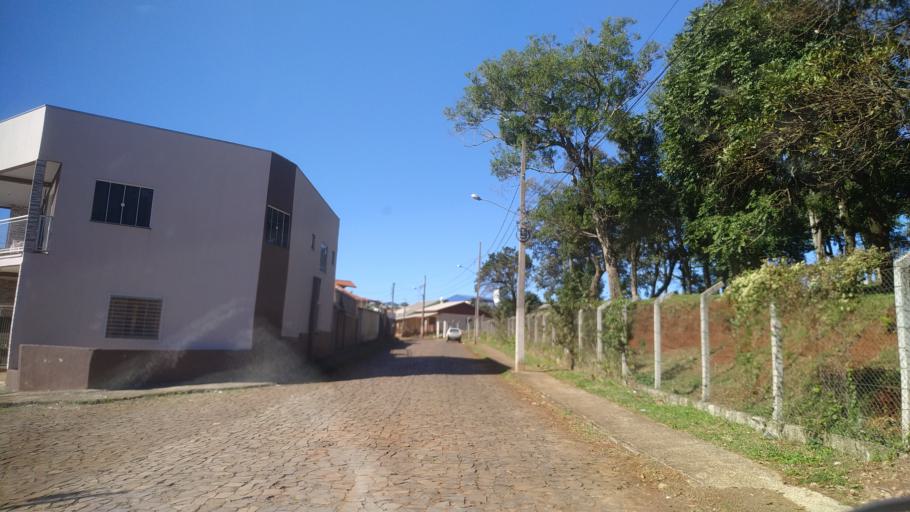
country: BR
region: Santa Catarina
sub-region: Chapeco
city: Chapeco
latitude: -27.1048
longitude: -52.6786
